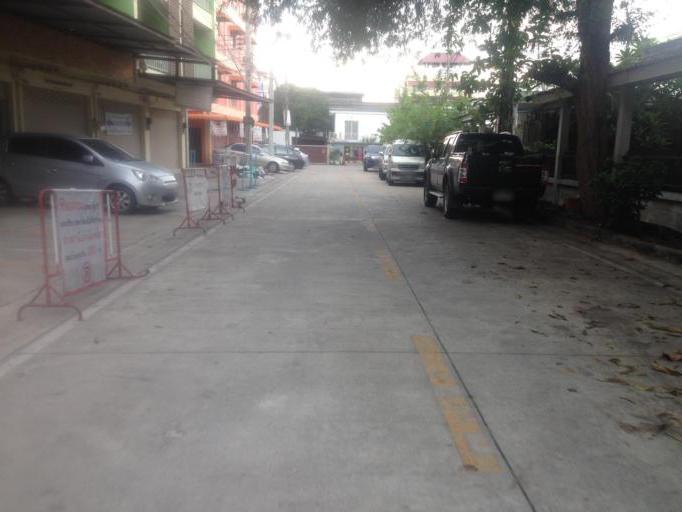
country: TH
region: Chon Buri
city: Chon Buri
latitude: 13.2879
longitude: 100.9297
